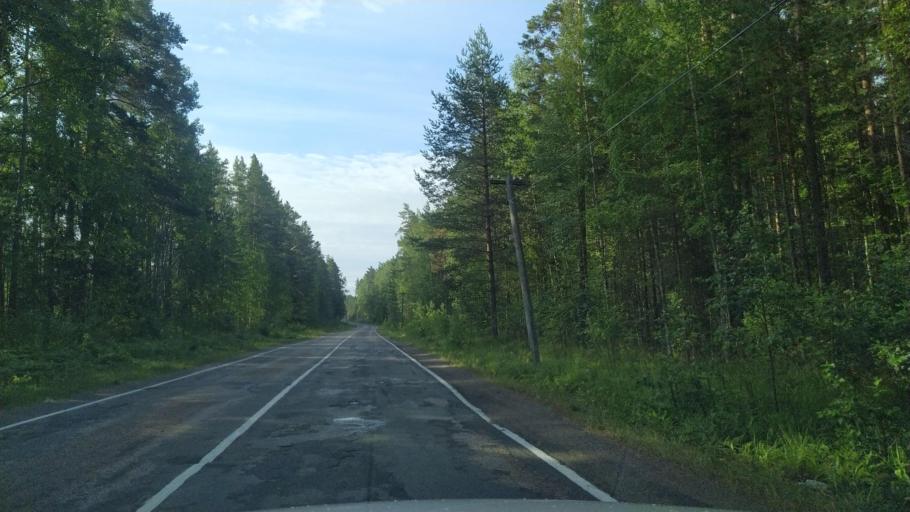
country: RU
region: Leningrad
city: Priozersk
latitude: 60.9857
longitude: 30.2653
